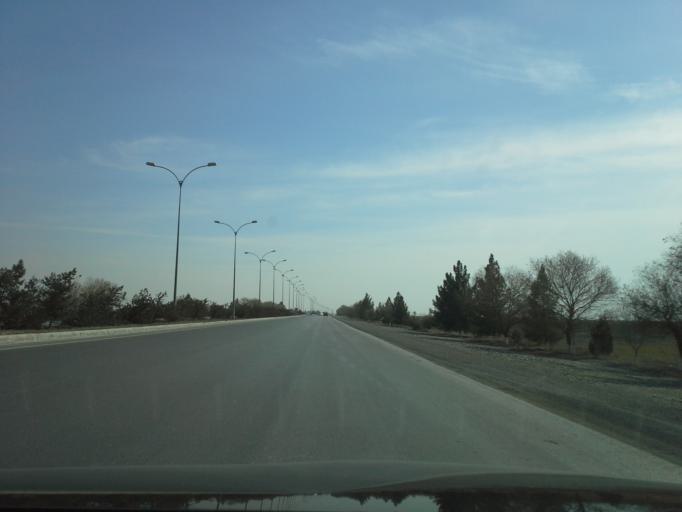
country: TM
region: Ahal
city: Abadan
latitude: 38.1267
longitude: 58.0307
